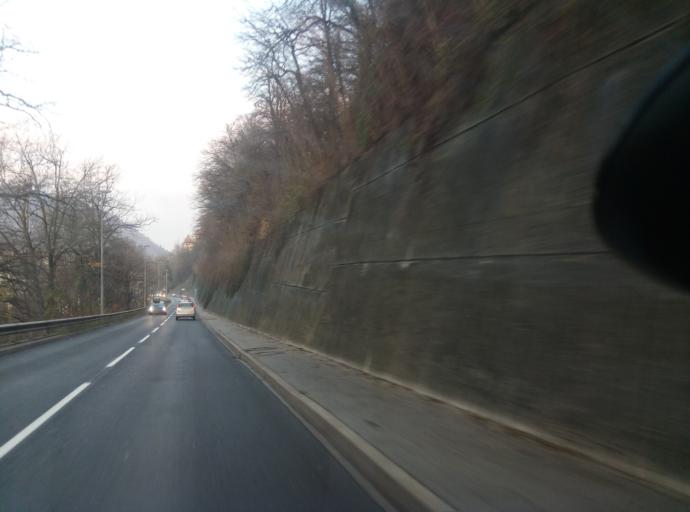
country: SI
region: Kranj
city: Kranj
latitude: 46.2326
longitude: 14.3609
